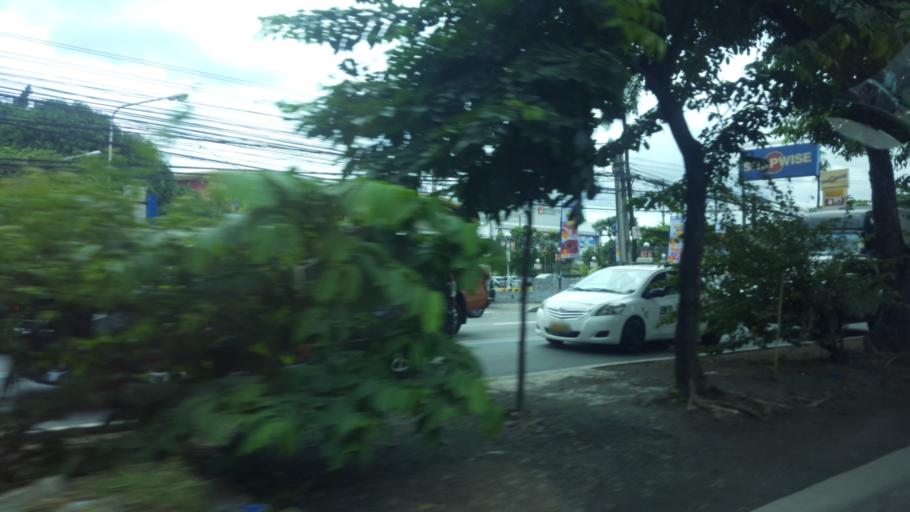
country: PH
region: Metro Manila
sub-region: Marikina
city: Calumpang
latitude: 14.6042
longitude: 121.0792
